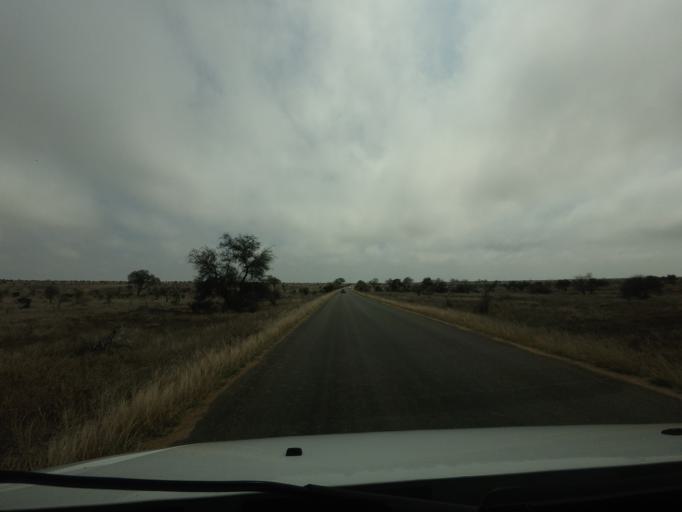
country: ZA
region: Limpopo
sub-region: Mopani District Municipality
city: Phalaborwa
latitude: -24.1972
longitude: 31.7188
